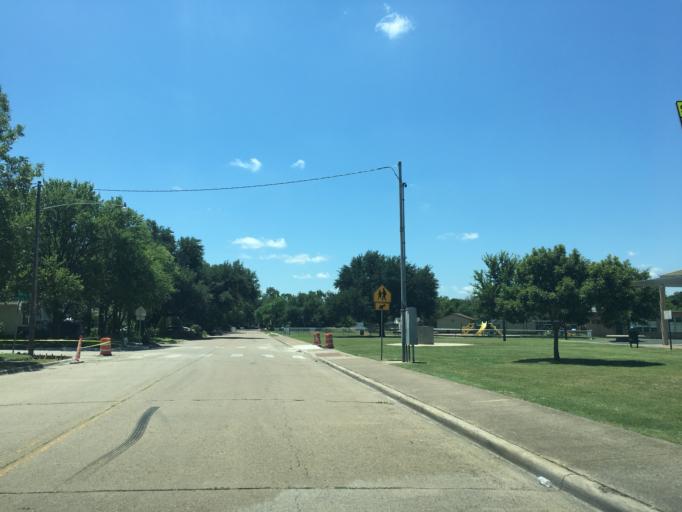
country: US
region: Texas
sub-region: Dallas County
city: Garland
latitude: 32.8469
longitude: -96.6742
